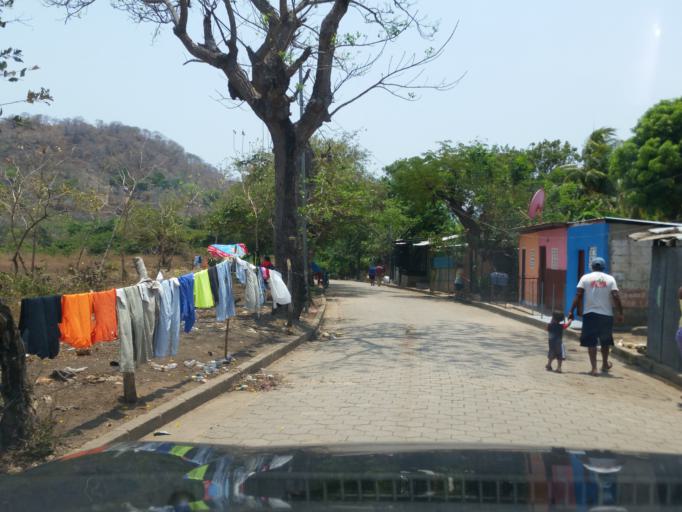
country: NI
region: Granada
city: Granada
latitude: 11.9098
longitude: -85.9534
